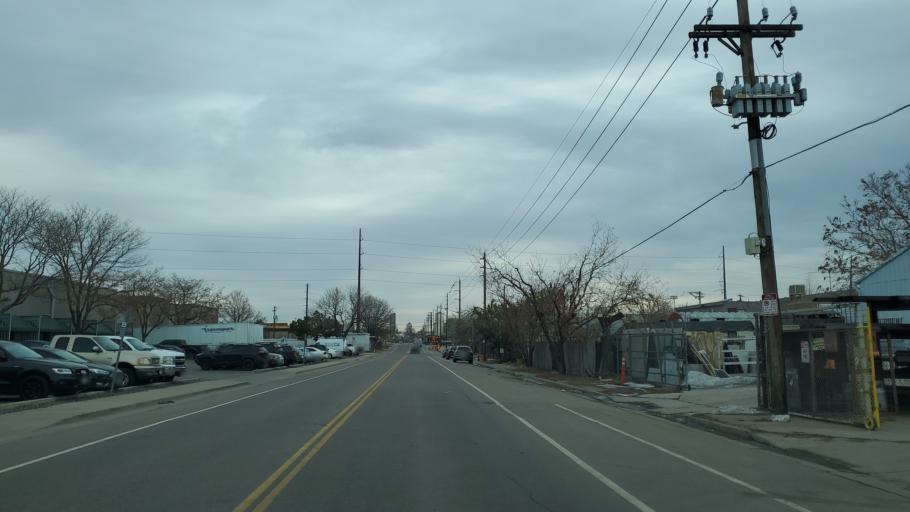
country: US
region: Colorado
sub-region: Denver County
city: Denver
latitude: 39.7148
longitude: -105.0079
